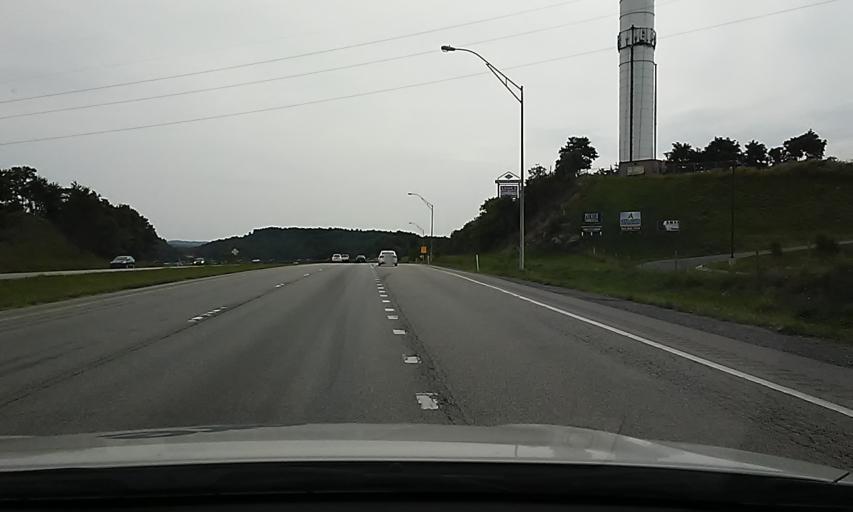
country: US
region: West Virginia
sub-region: Monongalia County
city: Brookhaven
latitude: 39.6509
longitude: -79.8918
